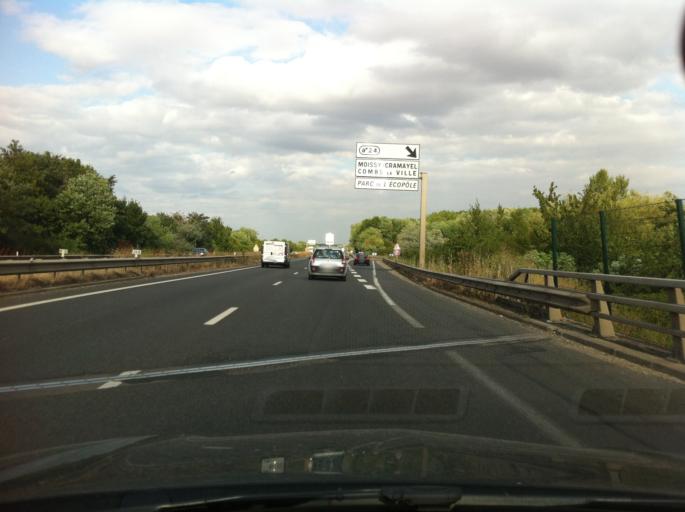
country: FR
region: Ile-de-France
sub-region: Departement de Seine-et-Marne
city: Combs-la-Ville
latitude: 48.6471
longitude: 2.5663
